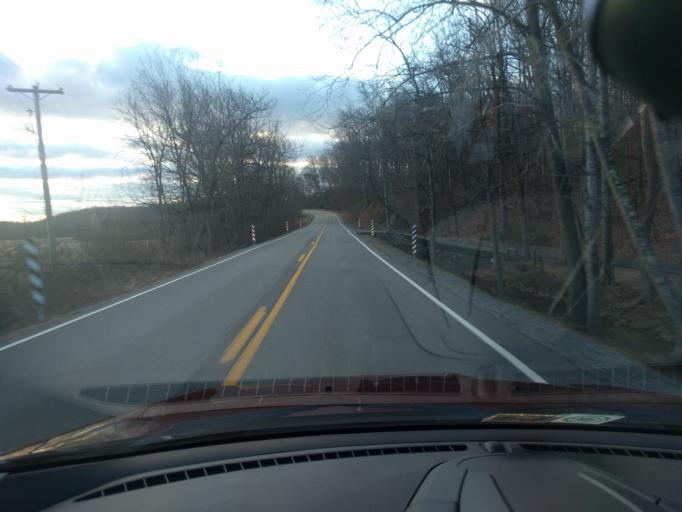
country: US
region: Virginia
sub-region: City of Bedford
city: Bedford
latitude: 37.4152
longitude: -79.5671
